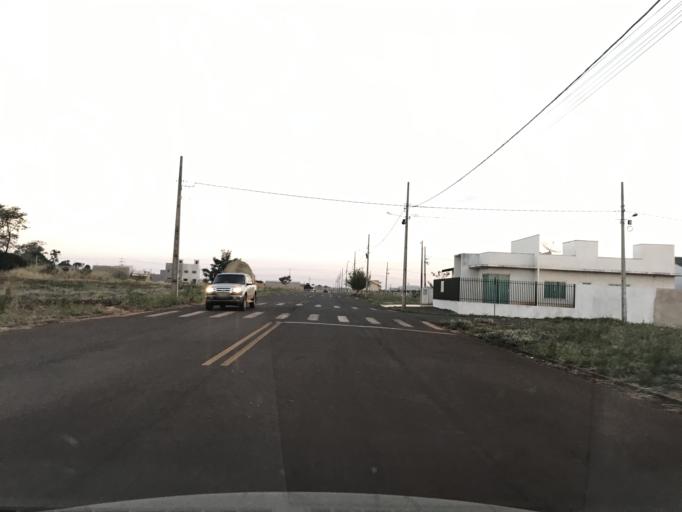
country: BR
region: Parana
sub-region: Palotina
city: Palotina
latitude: -24.3060
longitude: -53.8365
